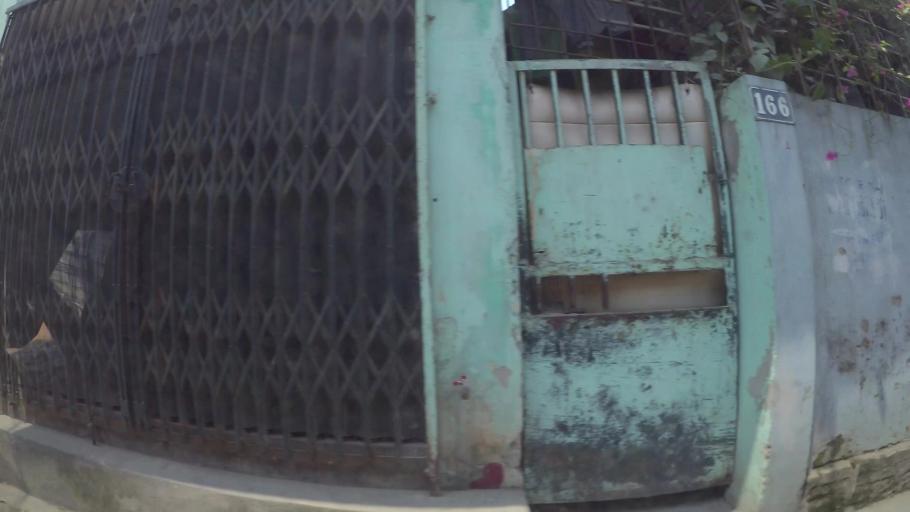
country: VN
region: Ha Noi
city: Van Dien
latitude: 20.9531
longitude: 105.8260
